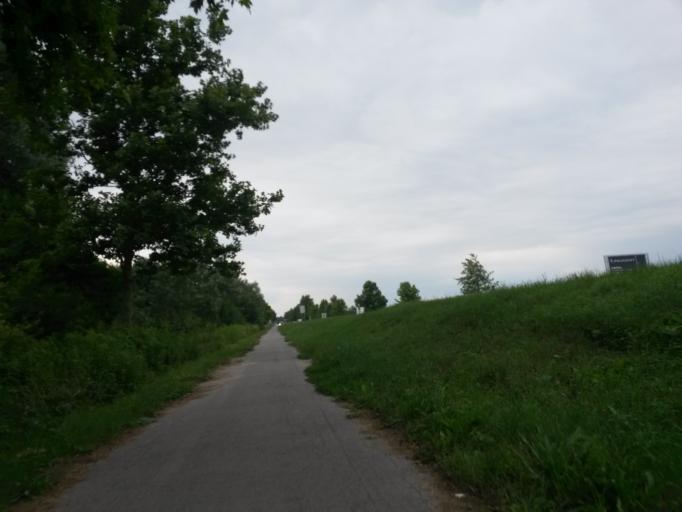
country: HR
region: Osjecko-Baranjska
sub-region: Grad Osijek
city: Osijek
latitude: 45.5755
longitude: 18.7169
